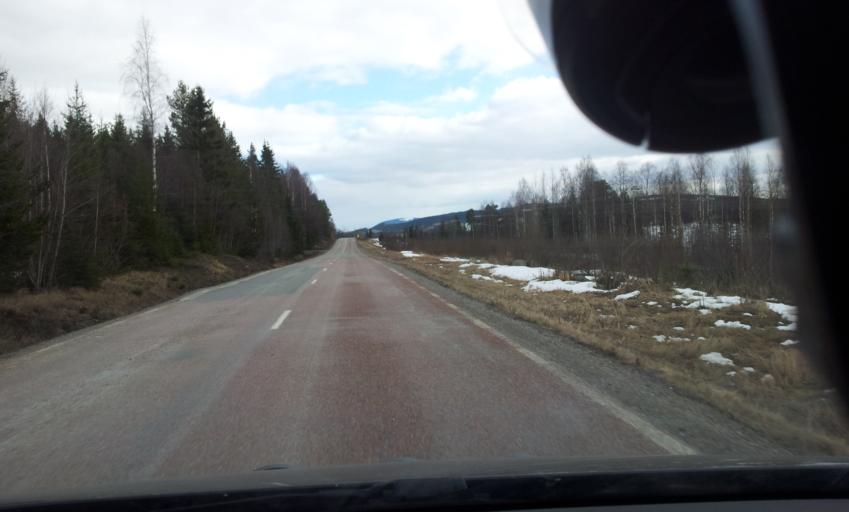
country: SE
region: Gaevleborg
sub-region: Ljusdals Kommun
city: Farila
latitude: 62.1371
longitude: 15.6908
